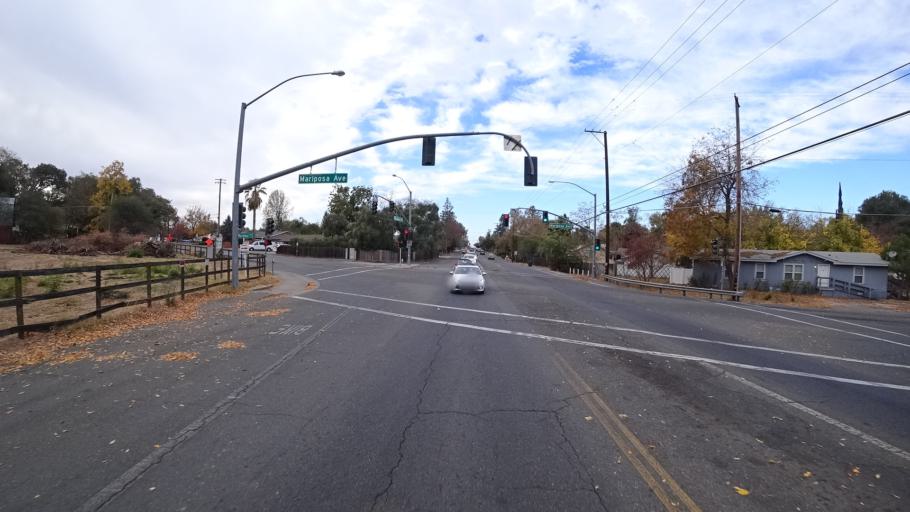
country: US
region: California
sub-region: Sacramento County
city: Citrus Heights
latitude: 38.6992
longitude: -121.2809
